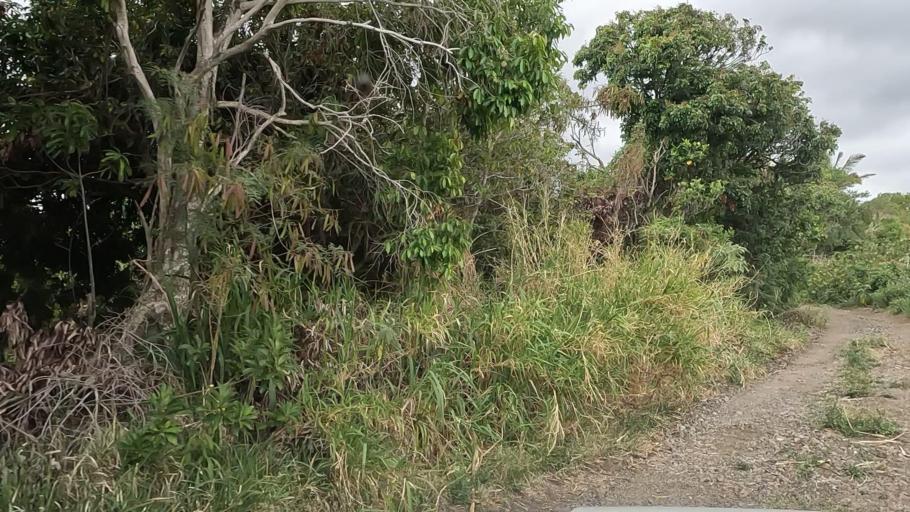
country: RE
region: Reunion
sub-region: Reunion
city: Saint-Pierre
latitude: -21.3387
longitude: 55.5222
